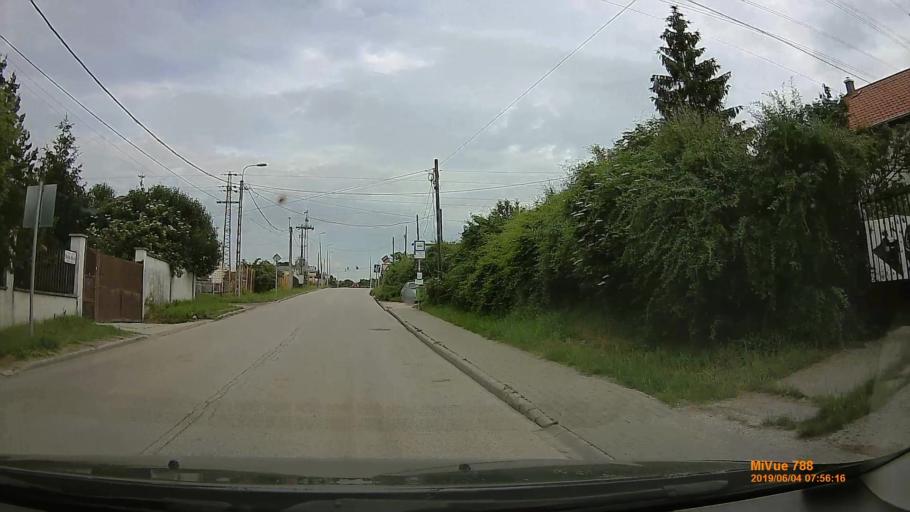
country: HU
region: Pest
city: Diosd
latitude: 47.4174
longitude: 18.9855
